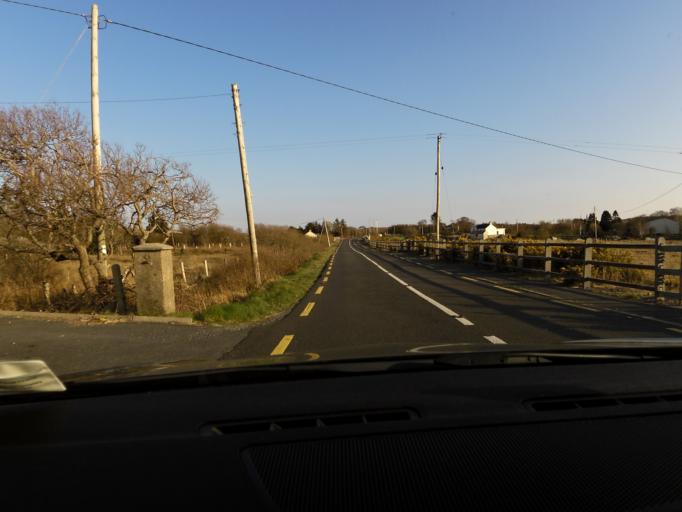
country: IE
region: Connaught
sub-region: County Galway
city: Oughterard
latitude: 53.3774
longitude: -9.5471
